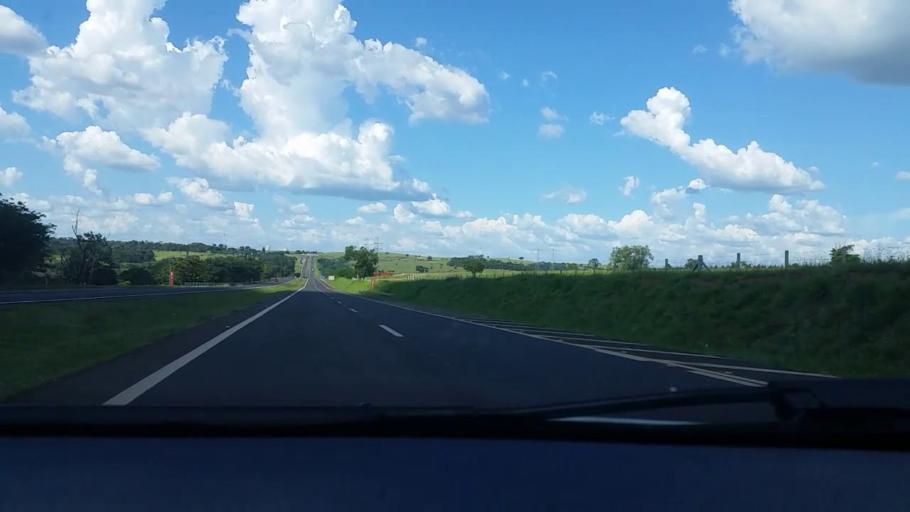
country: BR
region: Sao Paulo
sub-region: Bauru
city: Bauru
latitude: -22.4145
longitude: -49.1062
